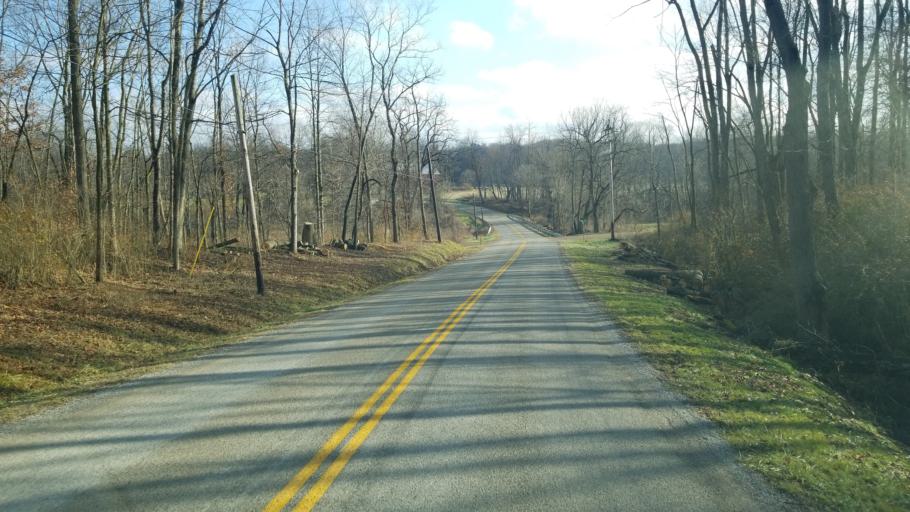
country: US
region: Ohio
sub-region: Ashland County
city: Ashland
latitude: 40.7628
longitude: -82.3478
